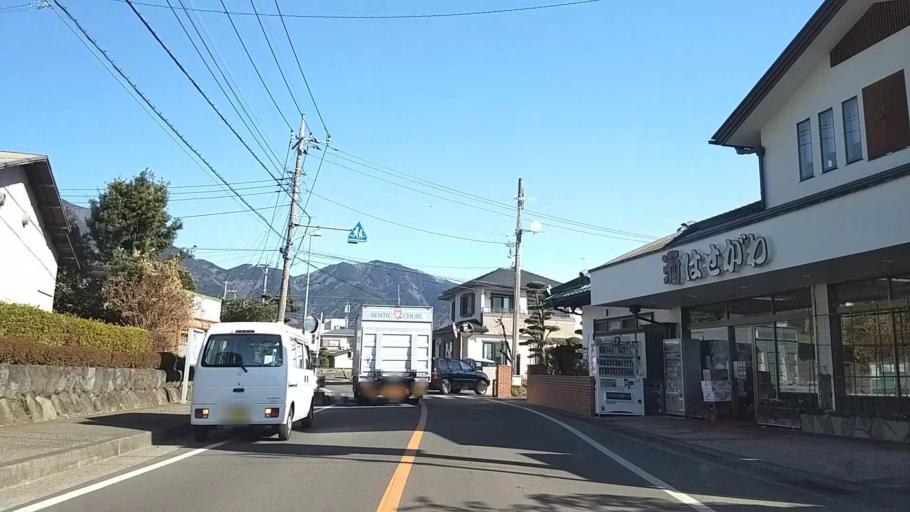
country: JP
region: Kanagawa
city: Hadano
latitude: 35.3956
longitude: 139.1830
